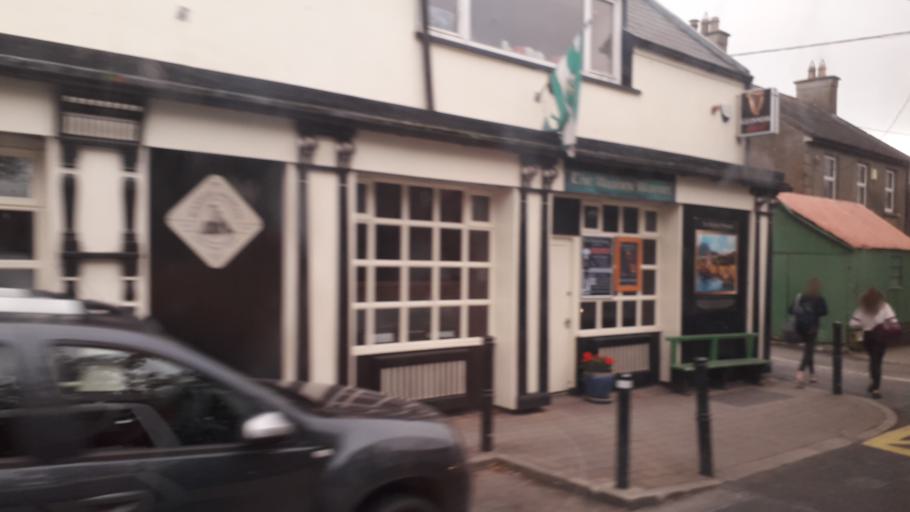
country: IE
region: Munster
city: Ballina
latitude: 52.8086
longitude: -8.4369
